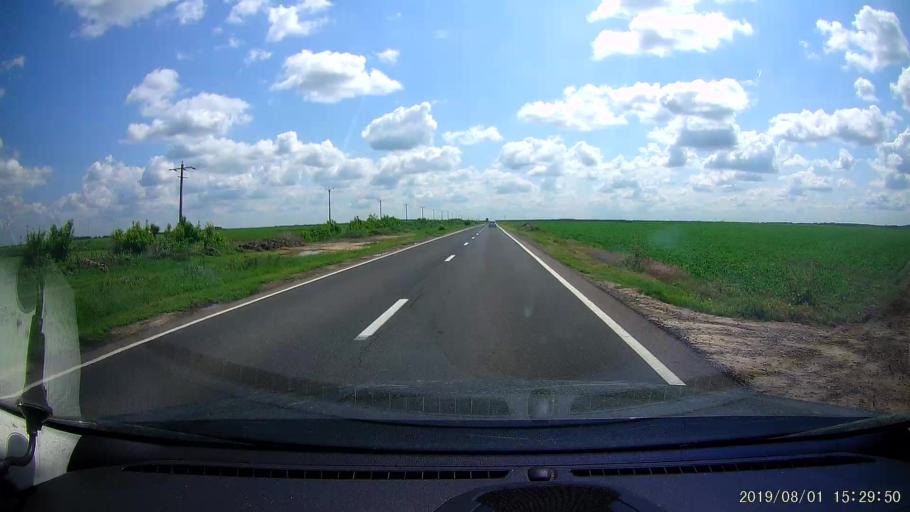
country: RO
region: Braila
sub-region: Comuna Viziru
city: Viziru
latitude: 44.9744
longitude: 27.6891
